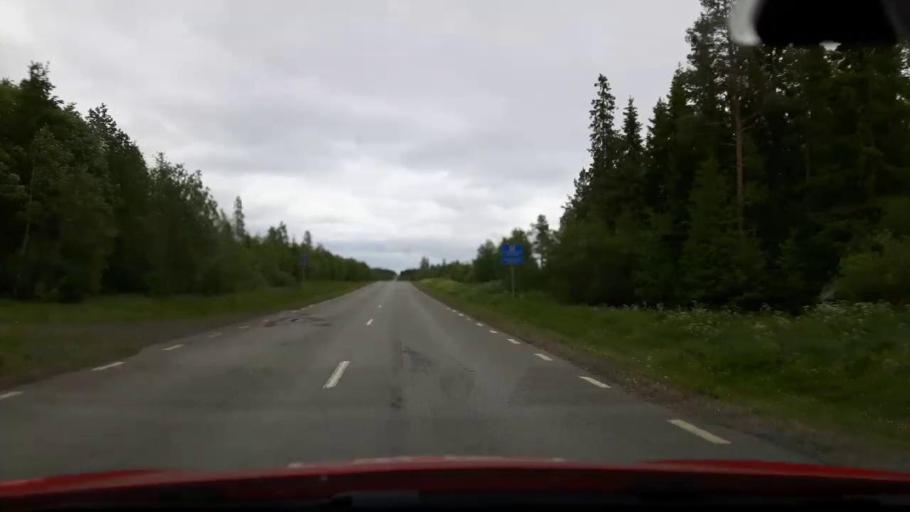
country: SE
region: Jaemtland
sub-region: OEstersunds Kommun
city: Lit
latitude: 63.7288
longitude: 14.9183
